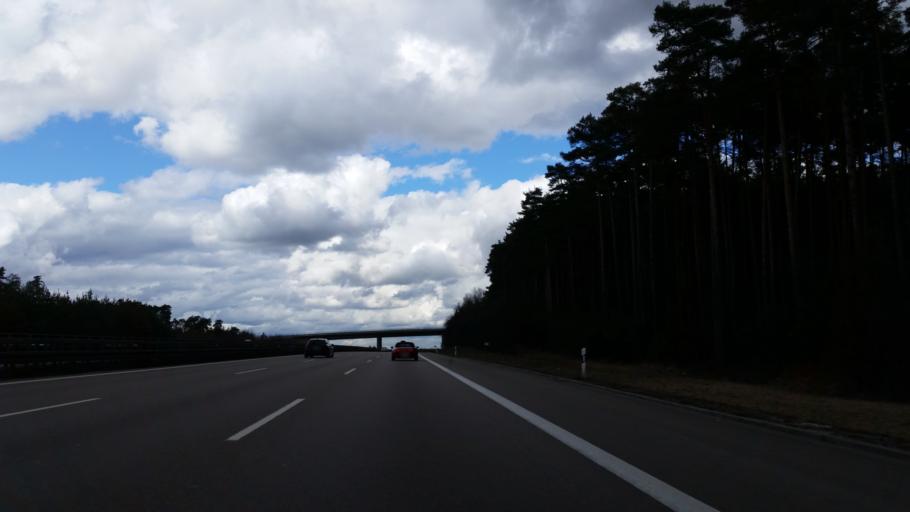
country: DE
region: Bavaria
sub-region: Regierungsbezirk Mittelfranken
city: Allersberg
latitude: 49.2768
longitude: 11.2101
